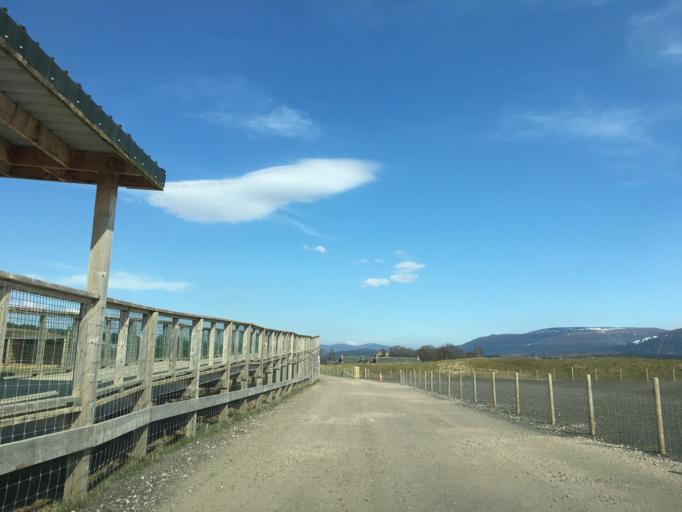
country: GB
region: Scotland
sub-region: Highland
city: Kingussie
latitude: 57.1074
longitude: -3.9710
